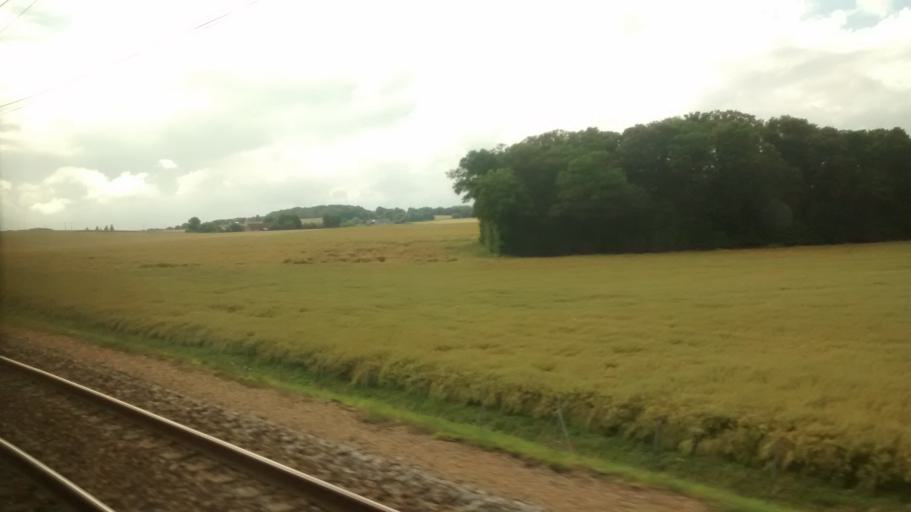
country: FR
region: Centre
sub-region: Departement du Loir-et-Cher
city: Droue
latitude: 48.0705
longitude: 1.0365
